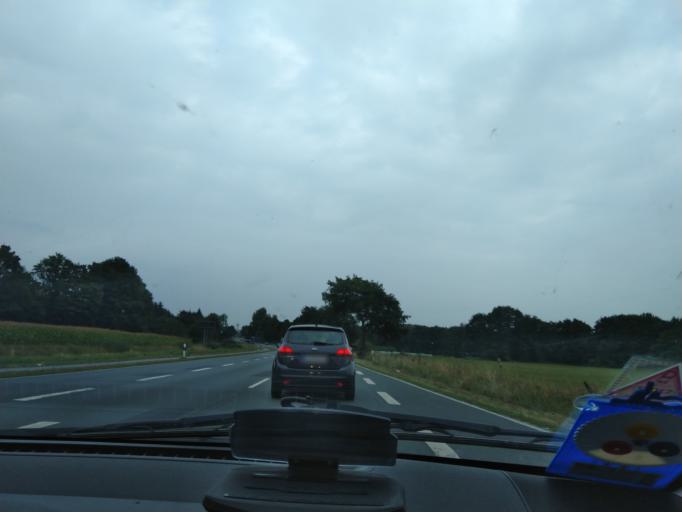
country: DE
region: Lower Saxony
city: Papenburg
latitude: 53.0793
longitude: 7.3795
